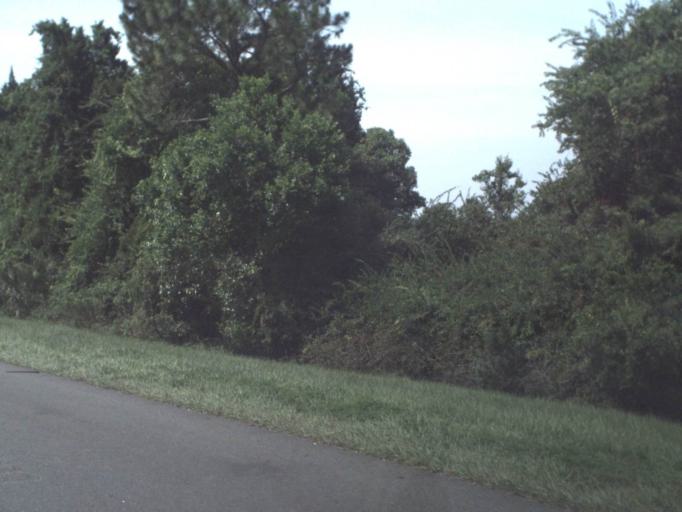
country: US
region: Florida
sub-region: Nassau County
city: Yulee
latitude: 30.5694
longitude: -81.6445
